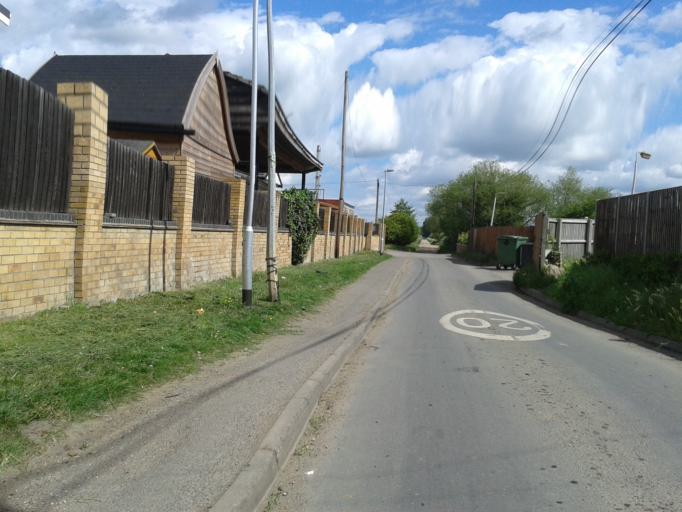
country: GB
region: England
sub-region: Cambridgeshire
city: Waterbeach
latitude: 52.2263
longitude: 0.1641
